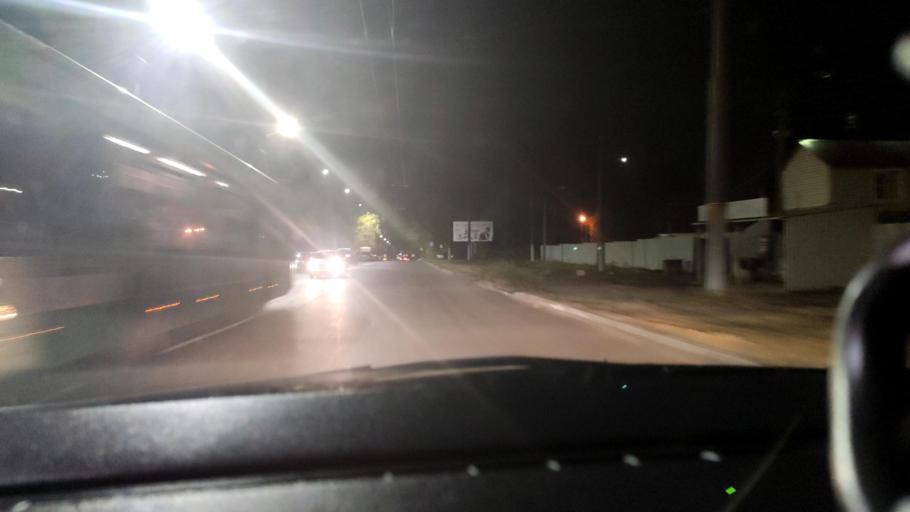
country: RU
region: Voronezj
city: Pridonskoy
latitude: 51.6527
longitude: 39.1009
